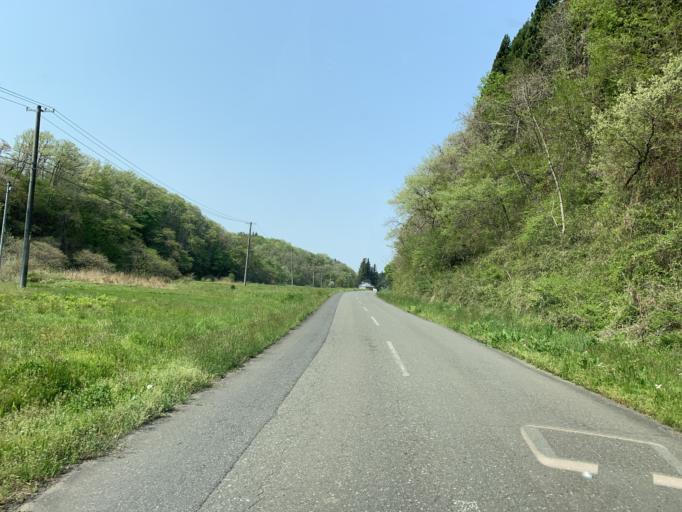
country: JP
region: Iwate
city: Ichinoseki
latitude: 38.8966
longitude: 141.0831
